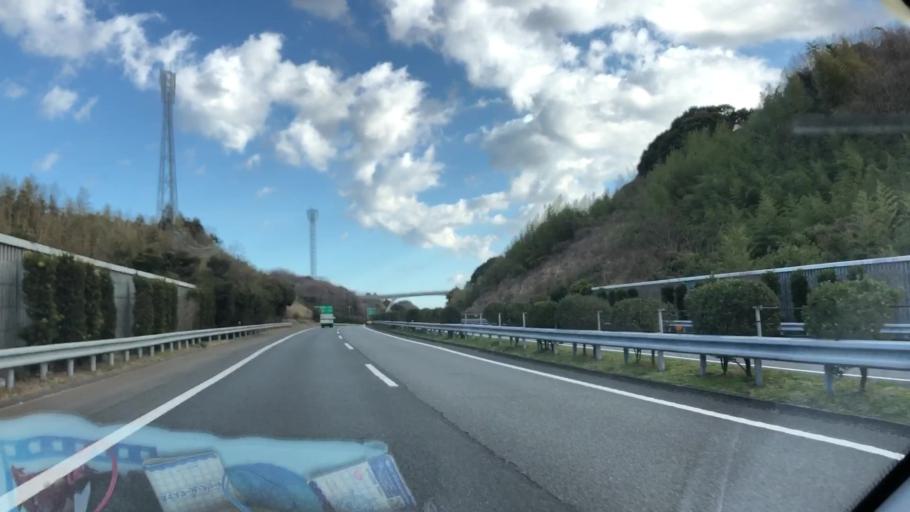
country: JP
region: Chiba
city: Kisarazu
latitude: 35.3646
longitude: 139.9601
